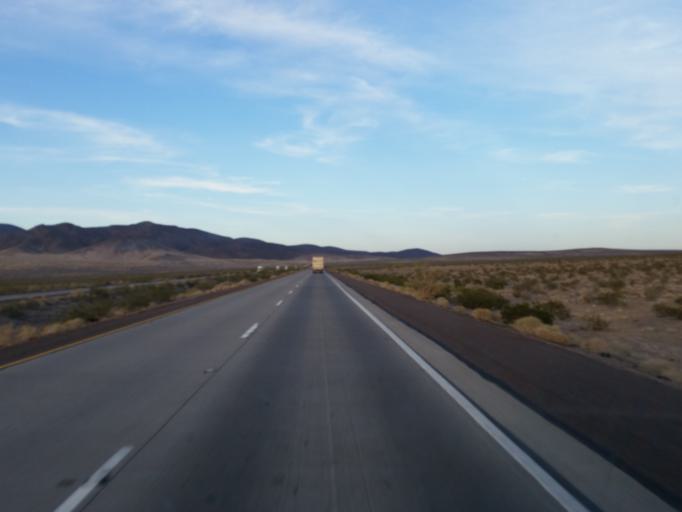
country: US
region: California
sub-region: San Bernardino County
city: Twentynine Palms
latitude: 34.7267
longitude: -116.1191
